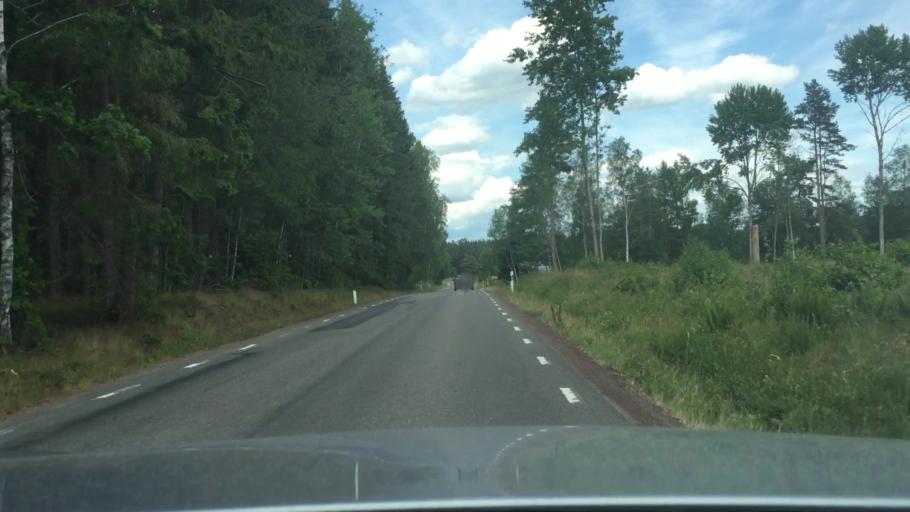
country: SE
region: Vaestra Goetaland
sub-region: Tidaholms Kommun
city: Tidaholm
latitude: 58.2055
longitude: 13.9814
